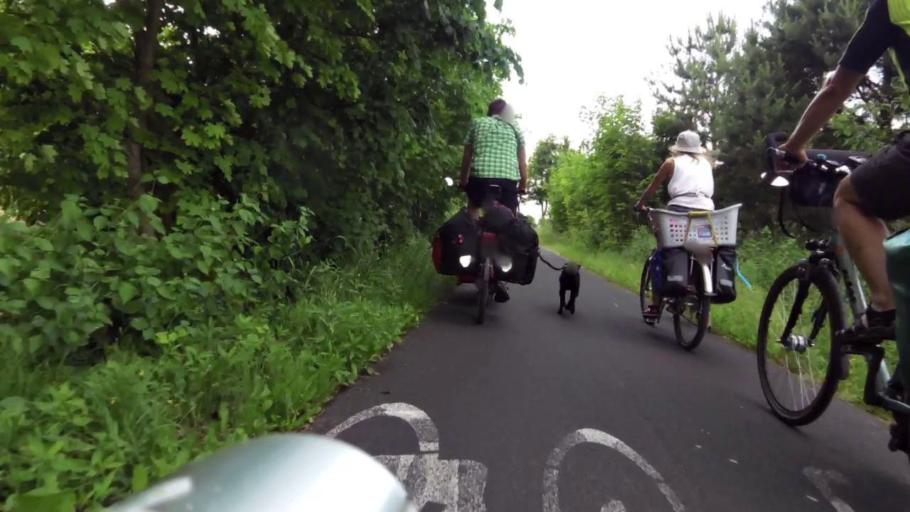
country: PL
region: Kujawsko-Pomorskie
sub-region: Powiat torunski
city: Lubianka
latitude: 53.0990
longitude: 18.5293
